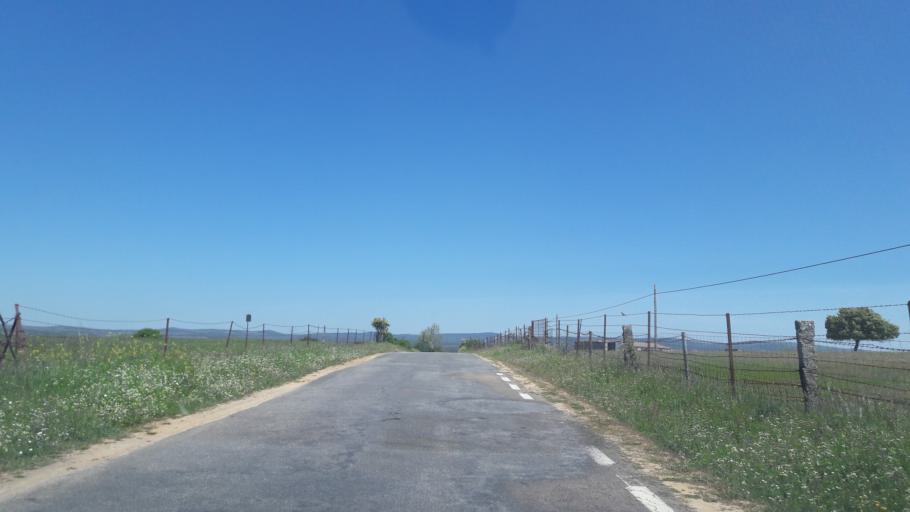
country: ES
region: Castille and Leon
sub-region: Provincia de Salamanca
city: Endrinal
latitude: 40.5797
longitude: -5.8083
